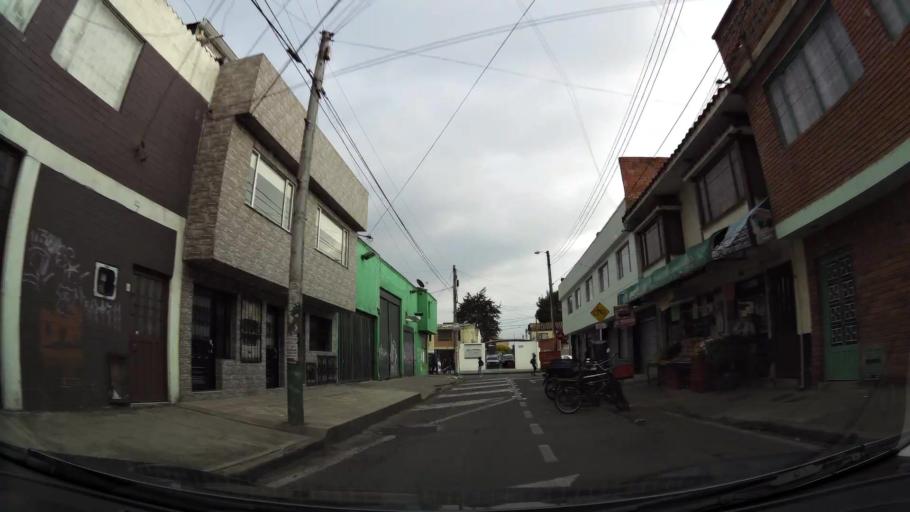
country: CO
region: Bogota D.C.
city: Barrio San Luis
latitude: 4.7196
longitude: -74.0716
